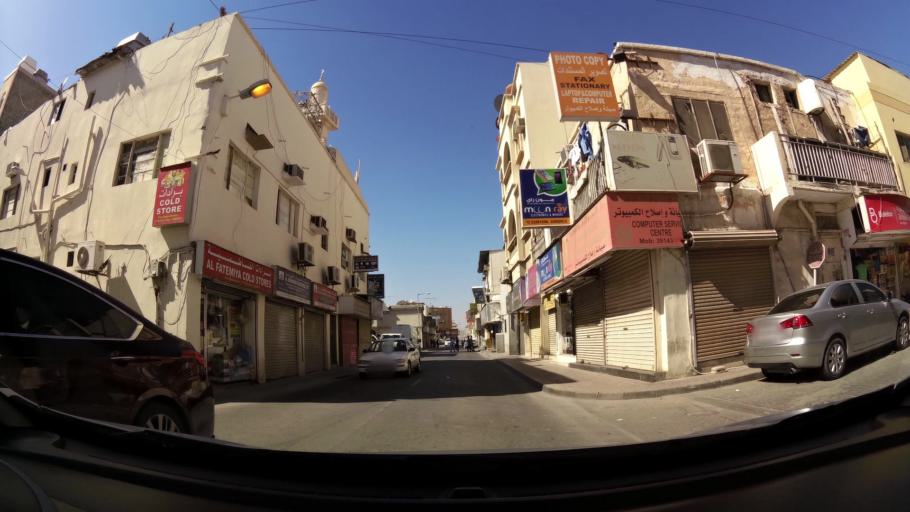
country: BH
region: Muharraq
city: Al Muharraq
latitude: 26.2476
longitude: 50.6145
